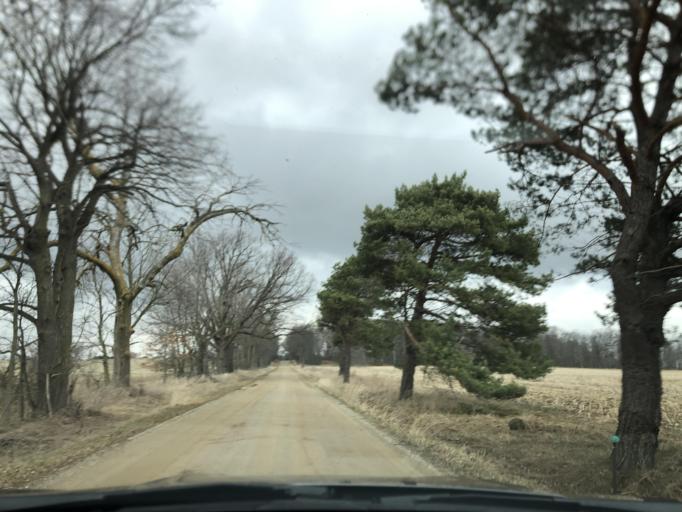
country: US
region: Michigan
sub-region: Clinton County
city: Saint Johns
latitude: 43.0977
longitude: -84.6106
